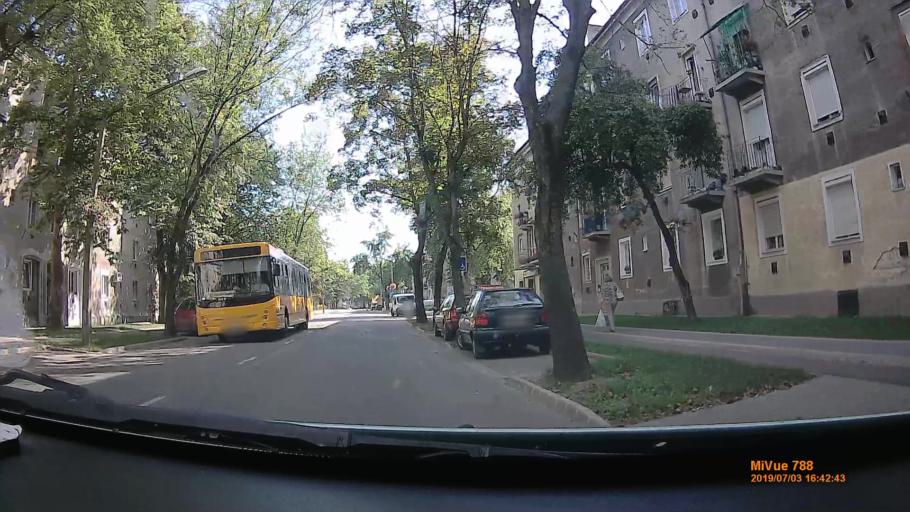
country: HU
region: Borsod-Abauj-Zemplen
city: Kazincbarcika
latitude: 48.2519
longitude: 20.6181
